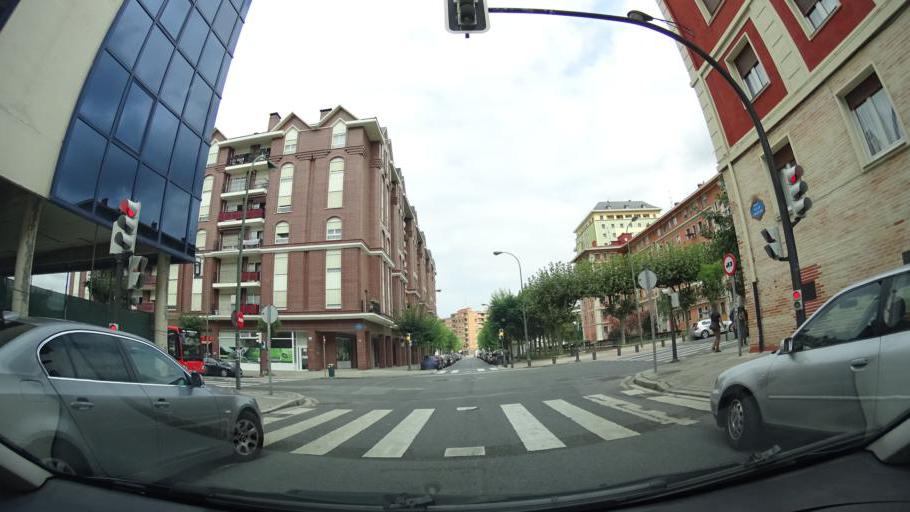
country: ES
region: Basque Country
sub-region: Bizkaia
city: Erandio
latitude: 43.2816
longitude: -2.9648
